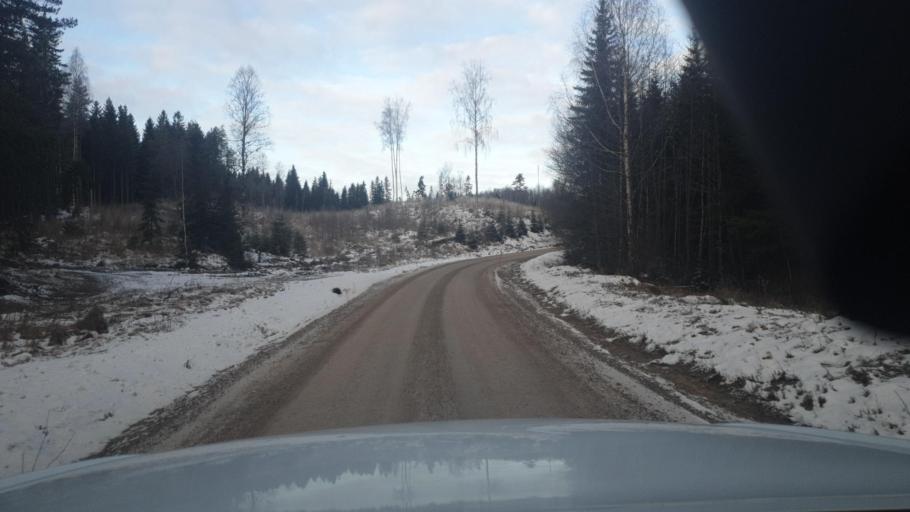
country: SE
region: Vaermland
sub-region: Arvika Kommun
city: Arvika
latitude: 59.9491
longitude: 12.6606
